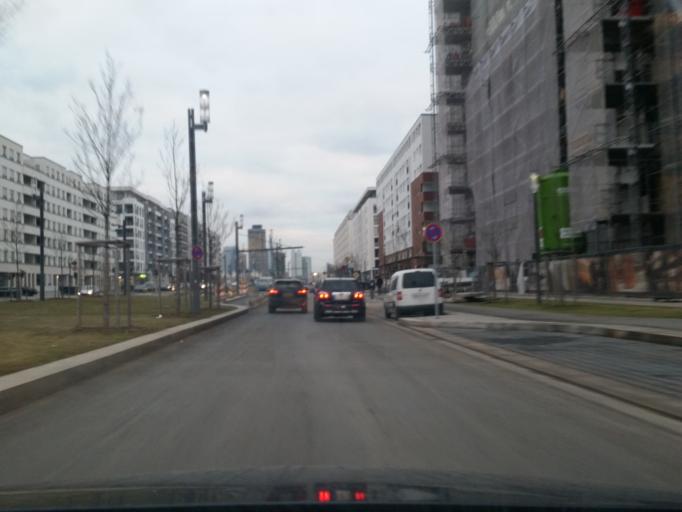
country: DE
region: Hesse
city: Niederrad
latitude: 50.1075
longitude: 8.6231
